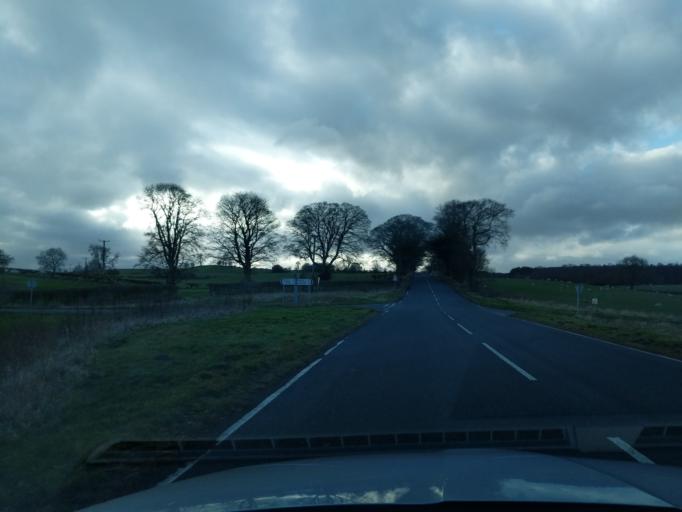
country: GB
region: England
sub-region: North Yorkshire
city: Catterick Garrison
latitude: 54.3462
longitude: -1.7157
